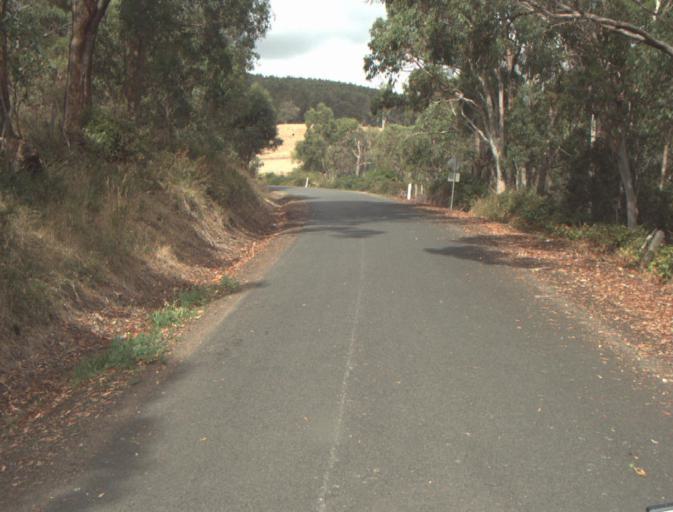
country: AU
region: Tasmania
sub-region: Dorset
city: Scottsdale
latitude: -41.4697
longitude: 147.5726
